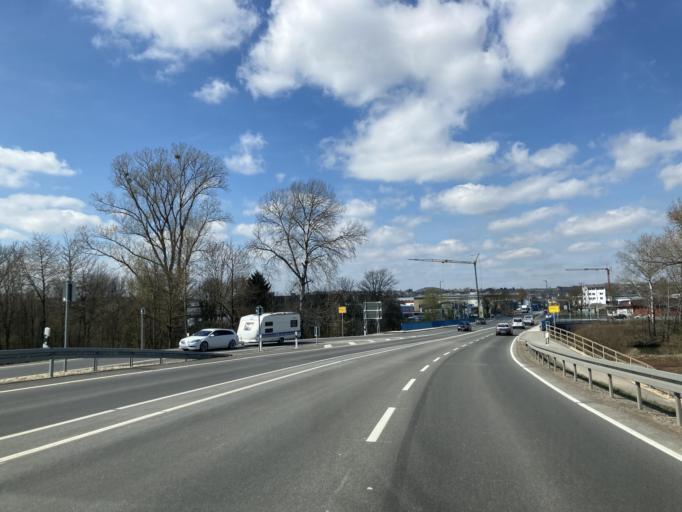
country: DE
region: Baden-Wuerttemberg
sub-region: Tuebingen Region
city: Rottenburg
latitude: 48.4751
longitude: 8.9568
